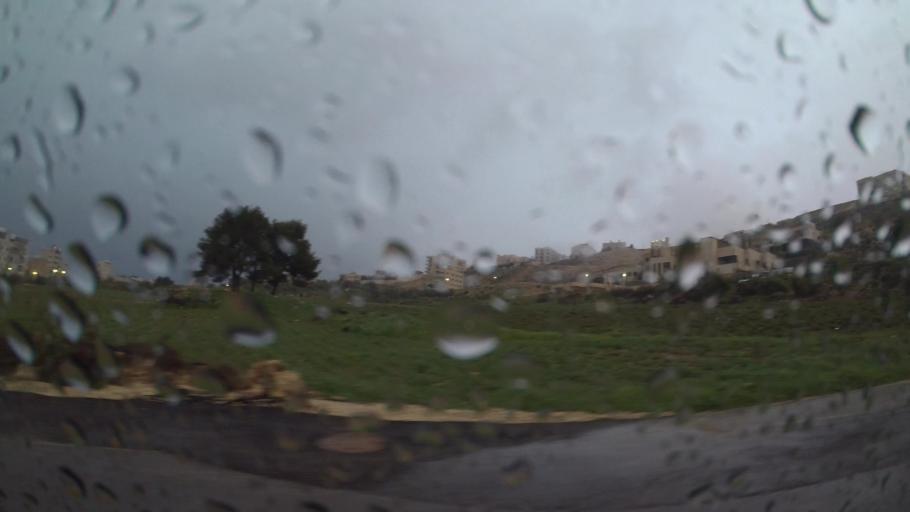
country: JO
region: Amman
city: Al Jubayhah
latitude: 32.0303
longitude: 35.8429
